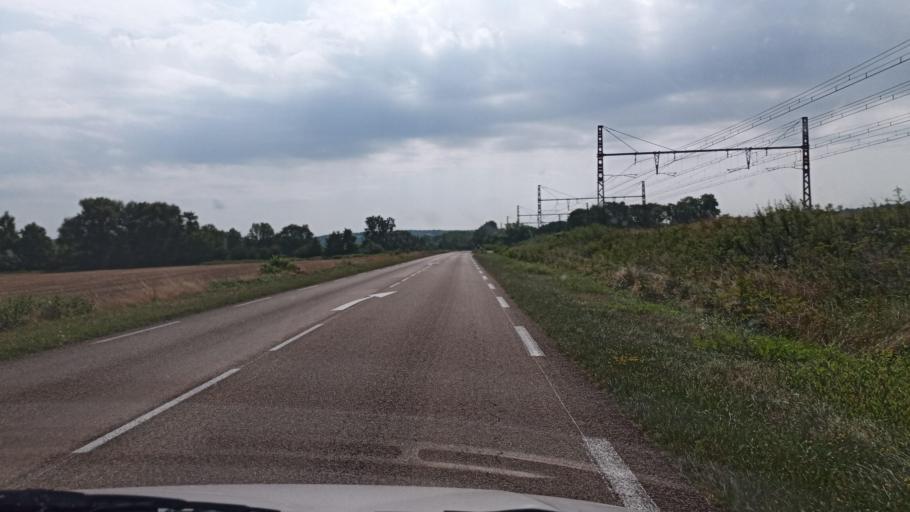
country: FR
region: Bourgogne
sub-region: Departement de l'Yonne
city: Villeneuve-sur-Yonne
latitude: 48.1022
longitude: 3.2727
